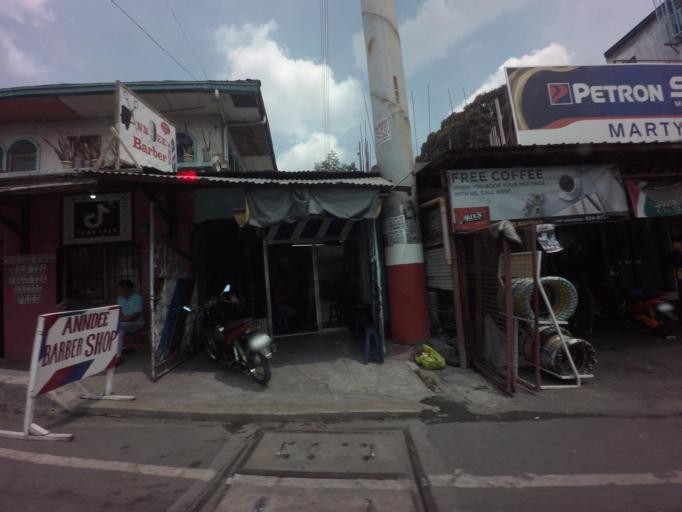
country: PH
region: Calabarzon
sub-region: Province of Rizal
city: Taguig
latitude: 14.4905
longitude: 121.0613
